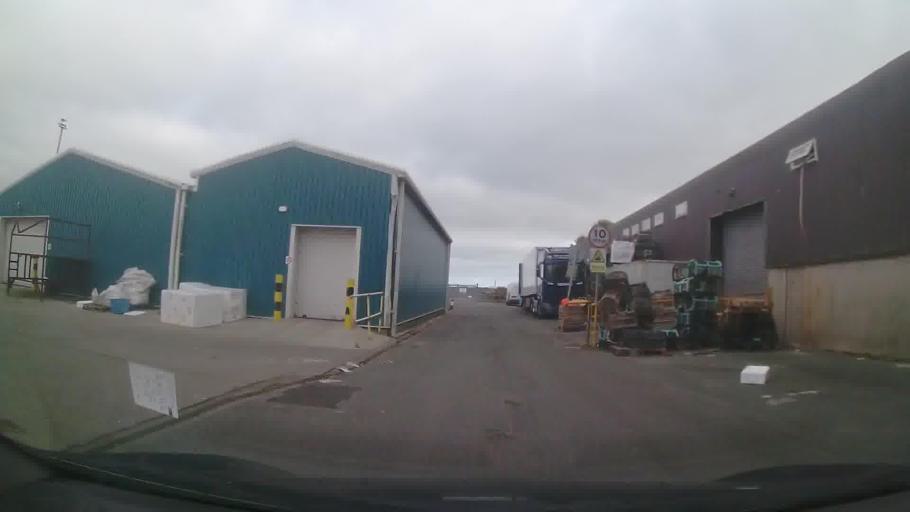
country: GB
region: Wales
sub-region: Pembrokeshire
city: Milford Haven
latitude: 51.7111
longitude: -5.0420
